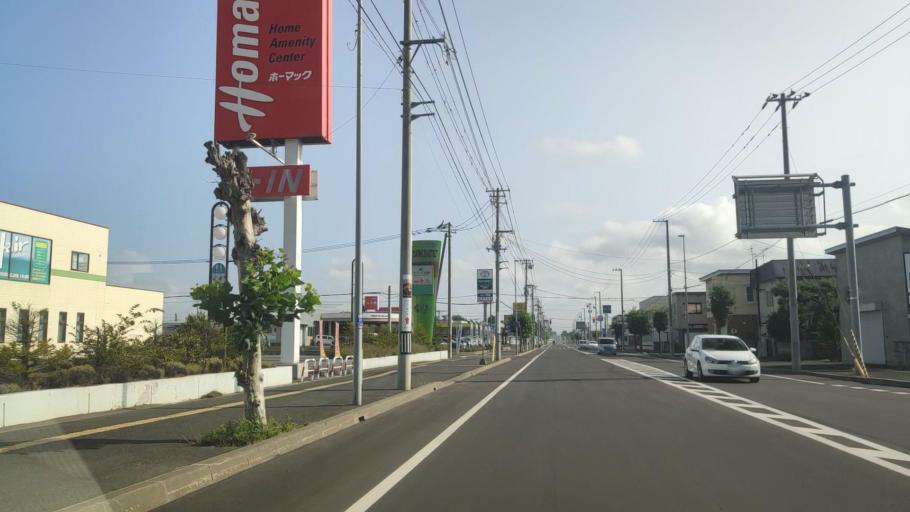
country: JP
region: Hokkaido
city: Shimo-furano
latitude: 43.3450
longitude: 142.3817
